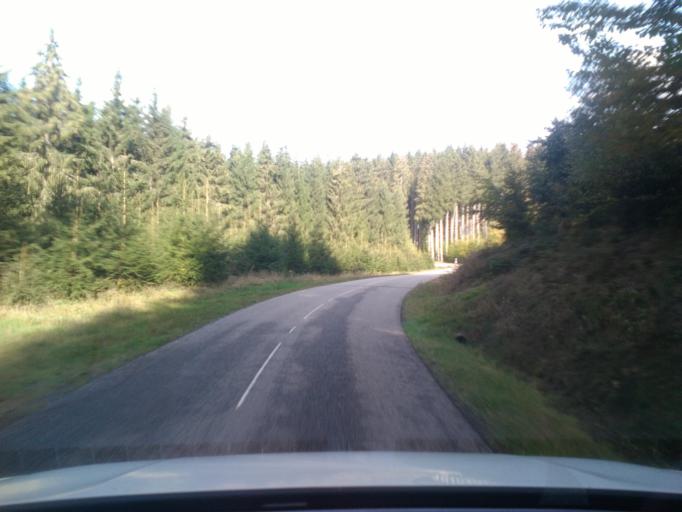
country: FR
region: Lorraine
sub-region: Departement des Vosges
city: Senones
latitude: 48.3802
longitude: 7.0555
